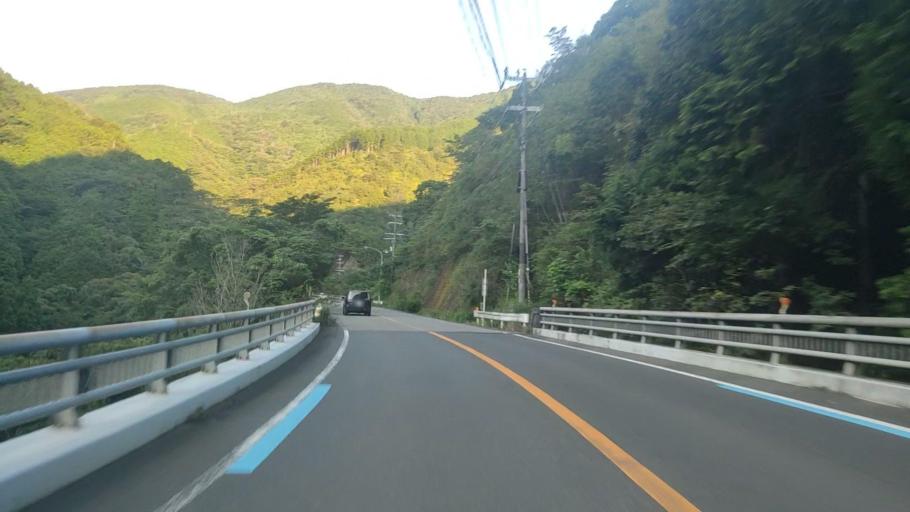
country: JP
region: Wakayama
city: Tanabe
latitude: 33.8143
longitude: 135.5619
